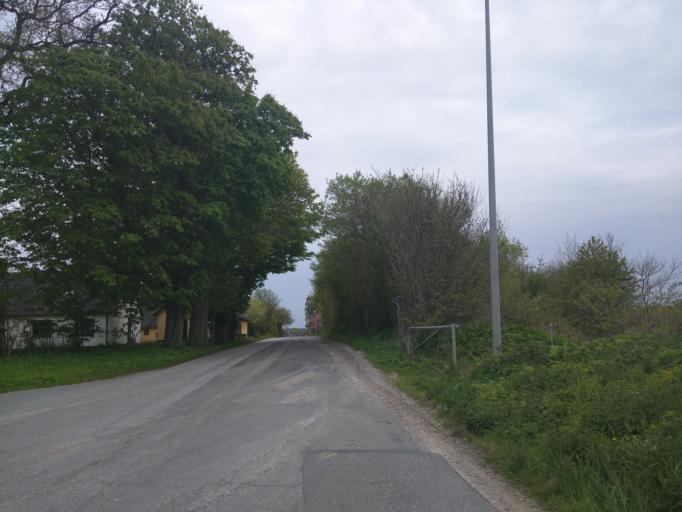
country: DK
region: South Denmark
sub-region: Fredericia Kommune
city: Snoghoj
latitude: 55.5330
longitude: 9.7053
